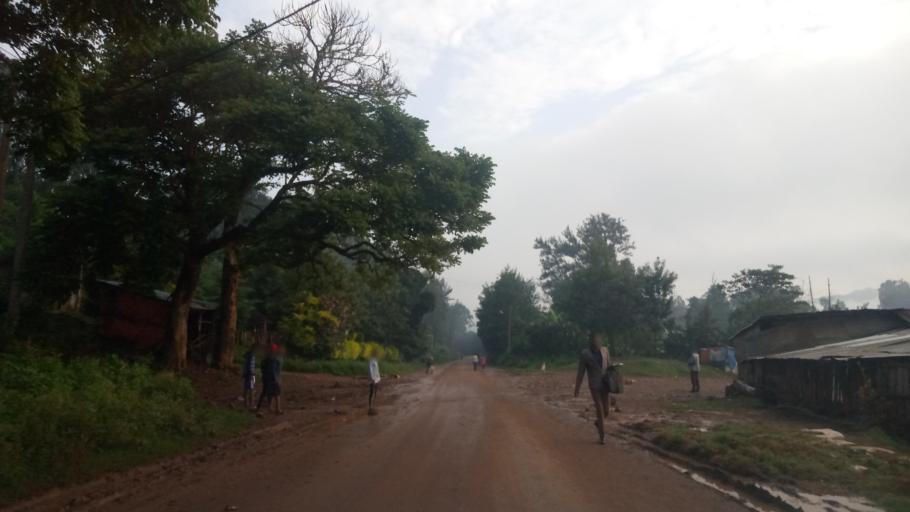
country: ET
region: Oromiya
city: Jima
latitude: 7.6822
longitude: 36.8338
